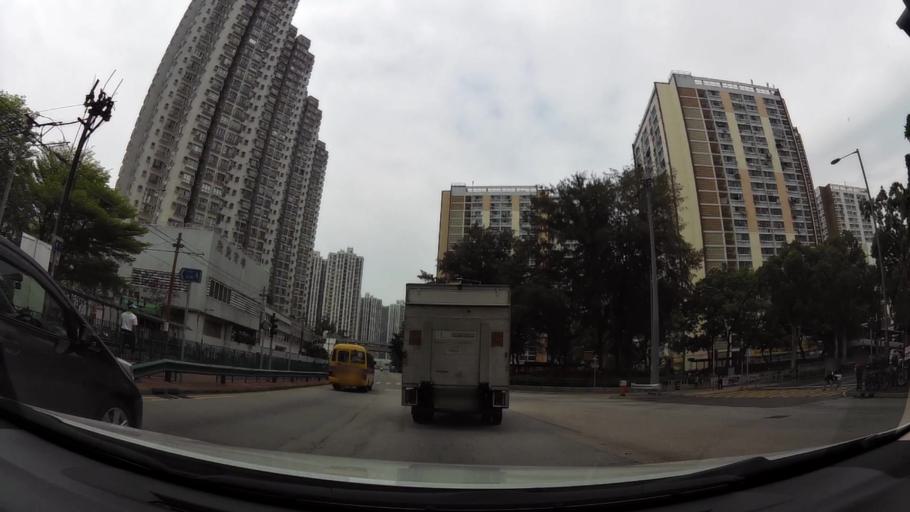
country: HK
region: Tuen Mun
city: Tuen Mun
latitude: 22.3732
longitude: 113.9658
